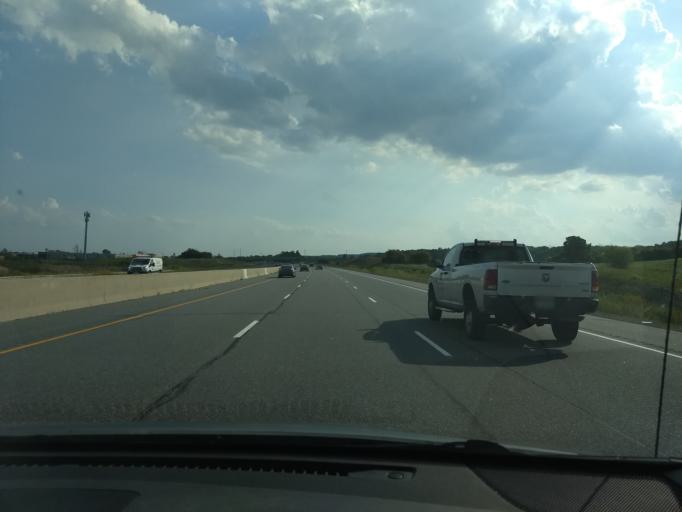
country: CA
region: Ontario
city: Burlington
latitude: 43.4051
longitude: -79.8304
